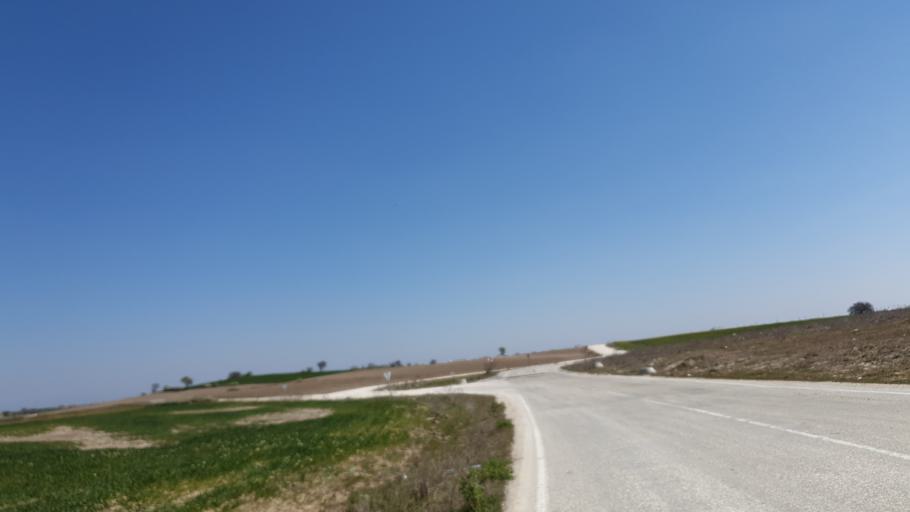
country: TR
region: Tekirdag
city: Cerkezkoey
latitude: 41.3235
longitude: 27.9336
